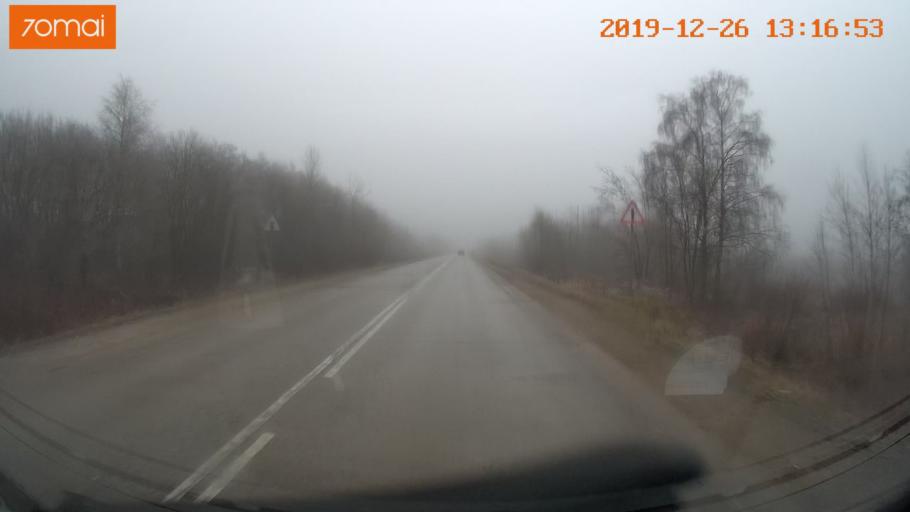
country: RU
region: Vologda
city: Cherepovets
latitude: 58.9762
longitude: 38.1101
